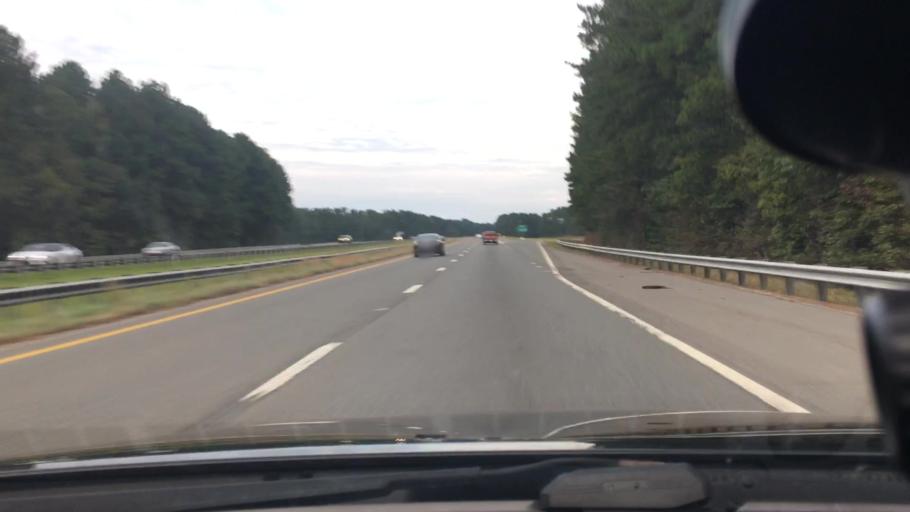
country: US
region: North Carolina
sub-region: Chatham County
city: Farmville
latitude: 35.5574
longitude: -79.1560
